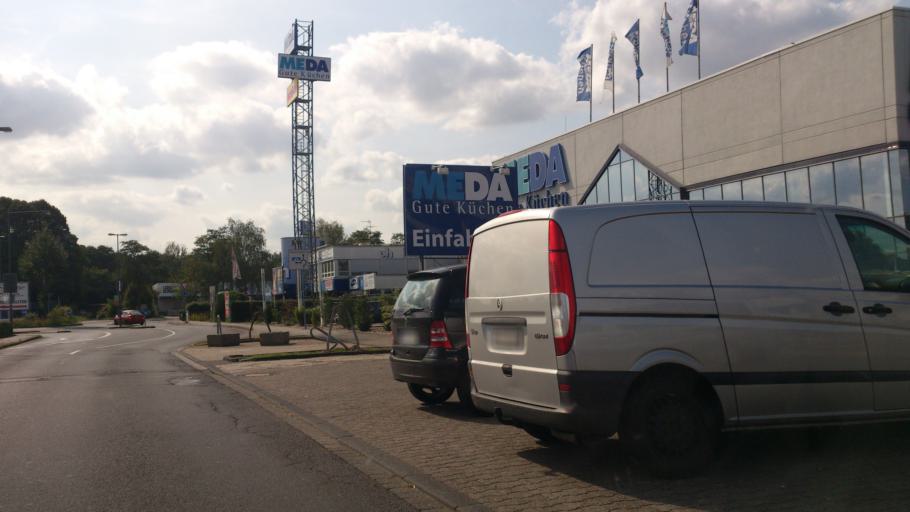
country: DE
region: North Rhine-Westphalia
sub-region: Regierungsbezirk Koln
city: Frechen
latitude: 50.9201
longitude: 6.8479
